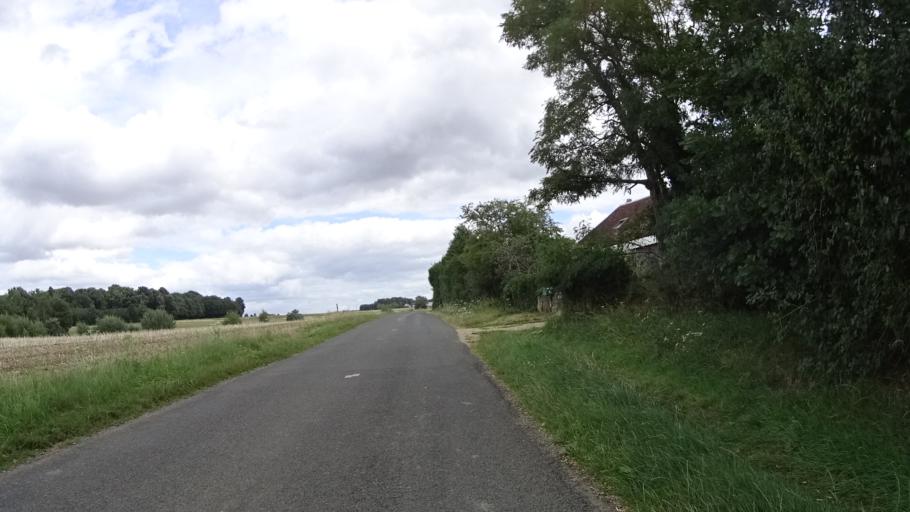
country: FR
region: Centre
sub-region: Departement du Loiret
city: Douchy
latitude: 47.9719
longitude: 3.0784
